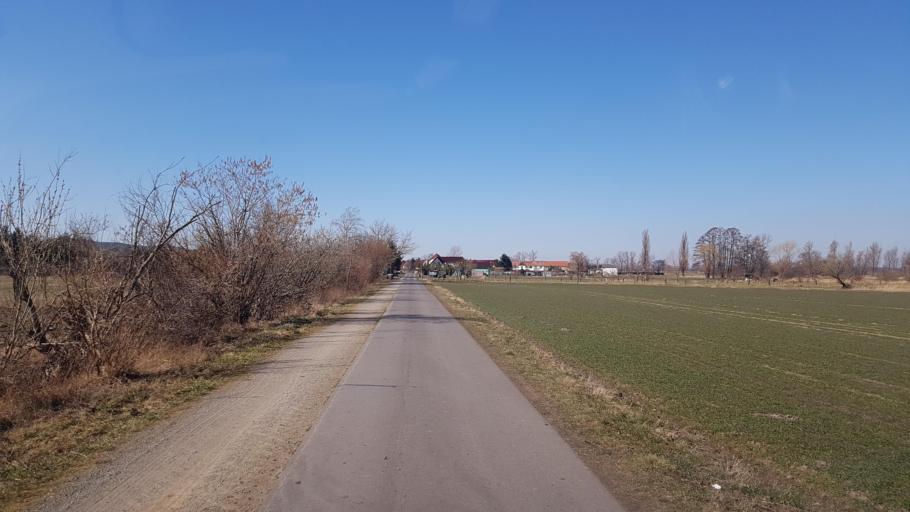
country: DE
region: Brandenburg
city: Hirschfeld
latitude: 51.3910
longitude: 13.6287
